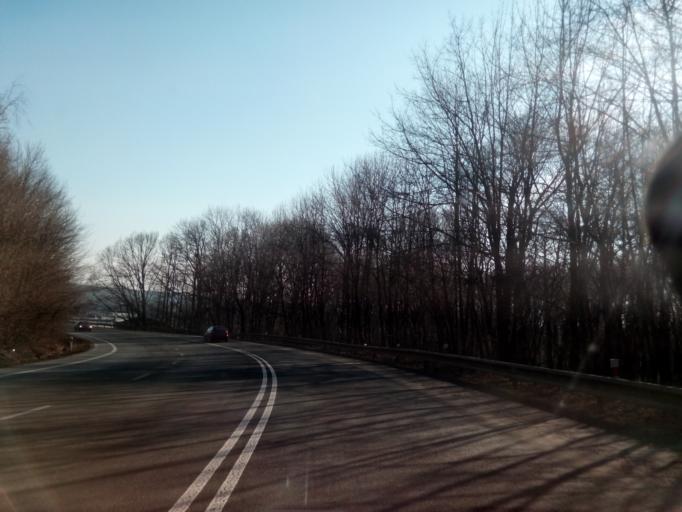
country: SK
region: Kosicky
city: Secovce
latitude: 48.7345
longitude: 21.5618
